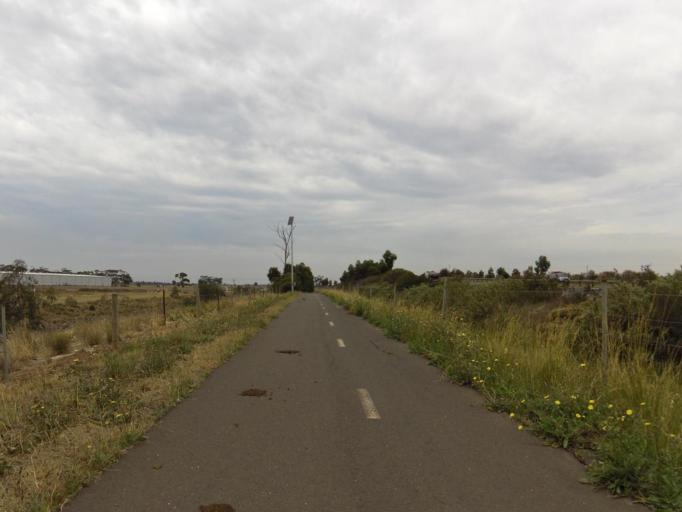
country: AU
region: Victoria
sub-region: Brimbank
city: Derrimut
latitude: -37.7771
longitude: 144.7473
